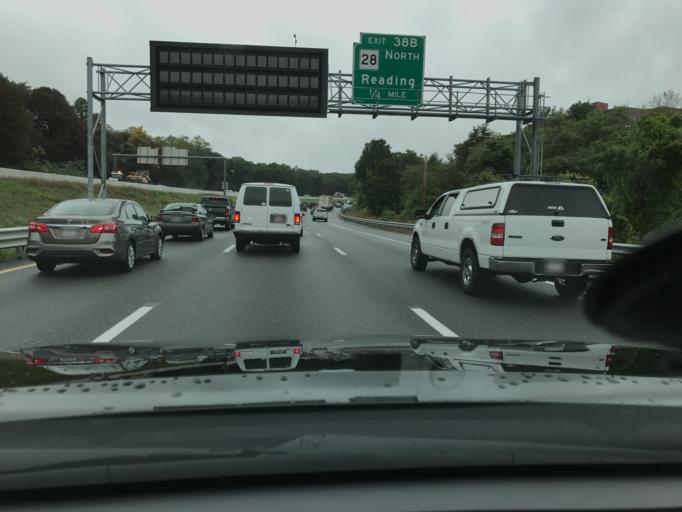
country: US
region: Massachusetts
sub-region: Middlesex County
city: Reading
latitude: 42.5088
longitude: -71.0935
